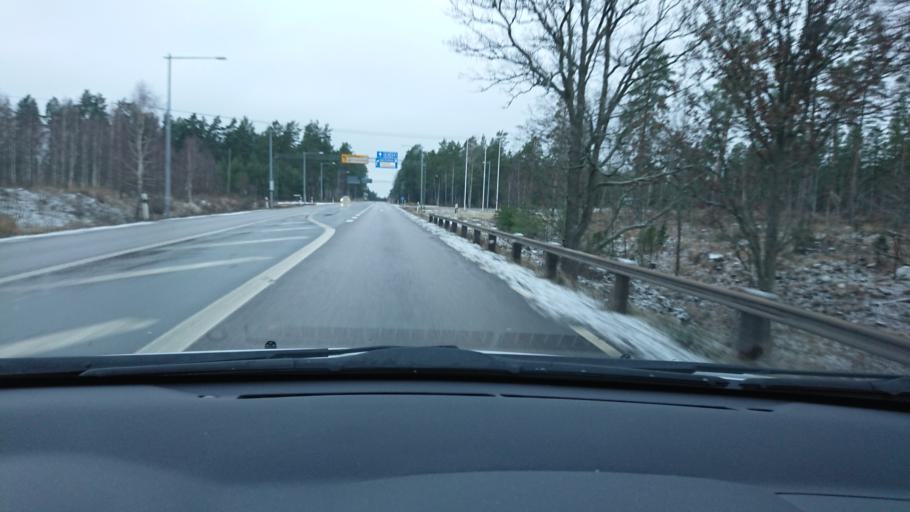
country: SE
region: Kalmar
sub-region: Hultsfreds Kommun
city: Hultsfred
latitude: 57.4877
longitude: 15.8275
